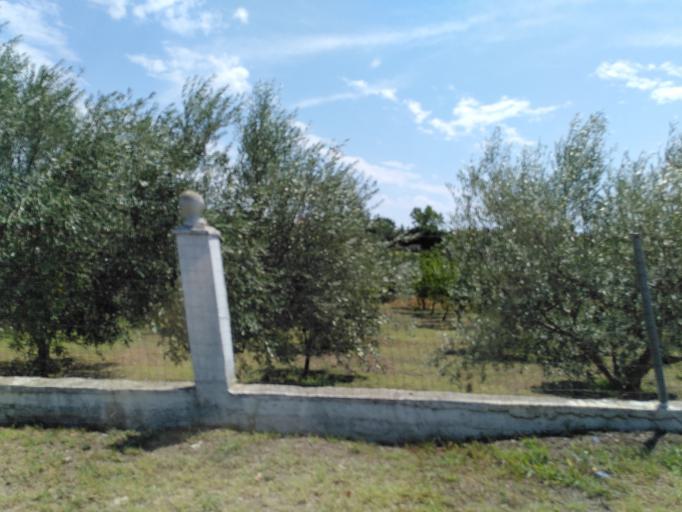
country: GR
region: Central Macedonia
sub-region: Nomos Thessalonikis
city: Nea Michaniona
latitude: 40.4292
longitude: 22.8835
